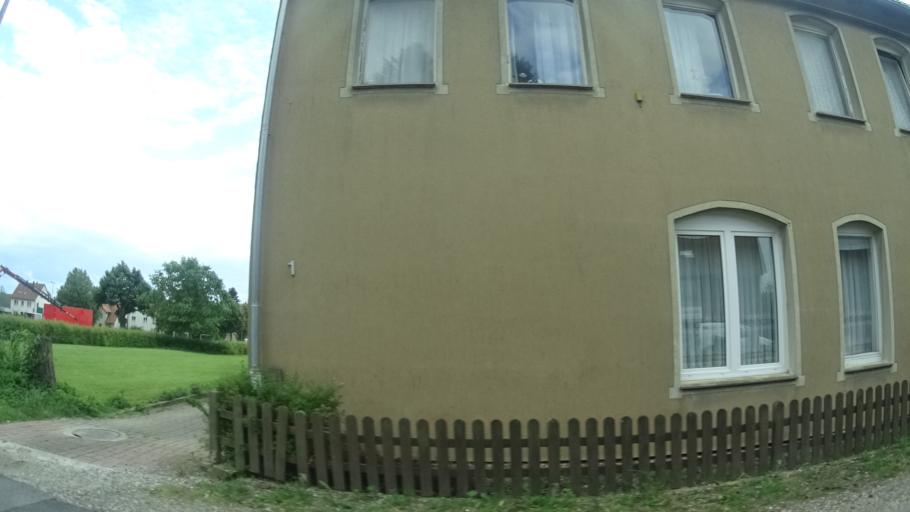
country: DE
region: Lower Saxony
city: Elze
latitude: 52.1716
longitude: 9.6496
